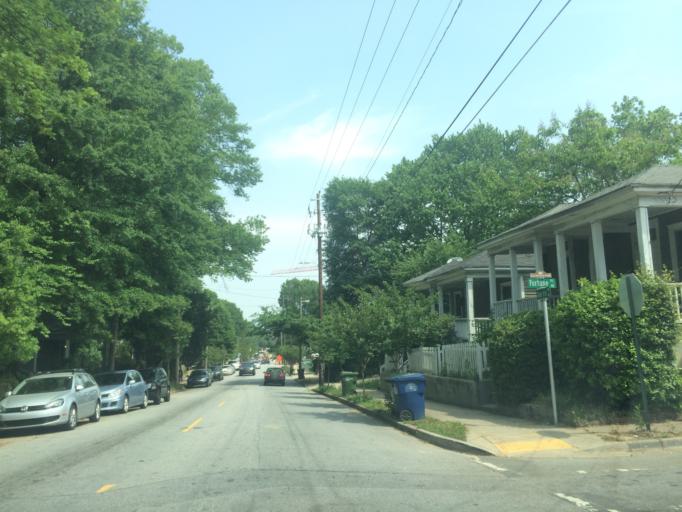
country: US
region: Georgia
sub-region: Fulton County
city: Atlanta
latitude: 33.7619
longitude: -84.3678
